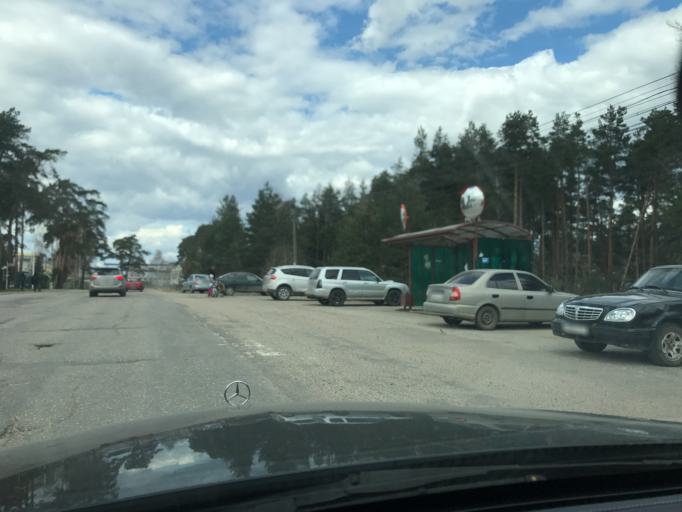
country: RU
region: Vladimir
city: Pokrov
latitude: 55.9022
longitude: 39.1943
